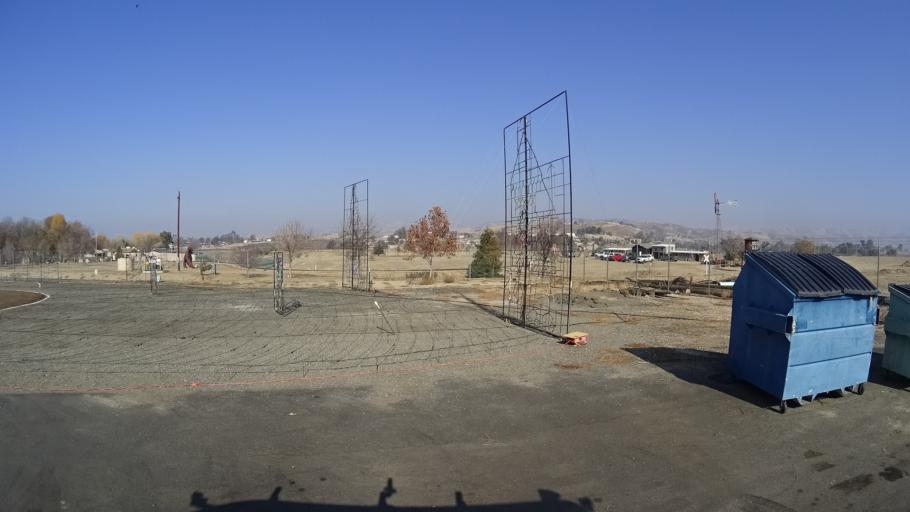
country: US
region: California
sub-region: Kern County
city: Oildale
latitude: 35.4319
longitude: -118.8840
